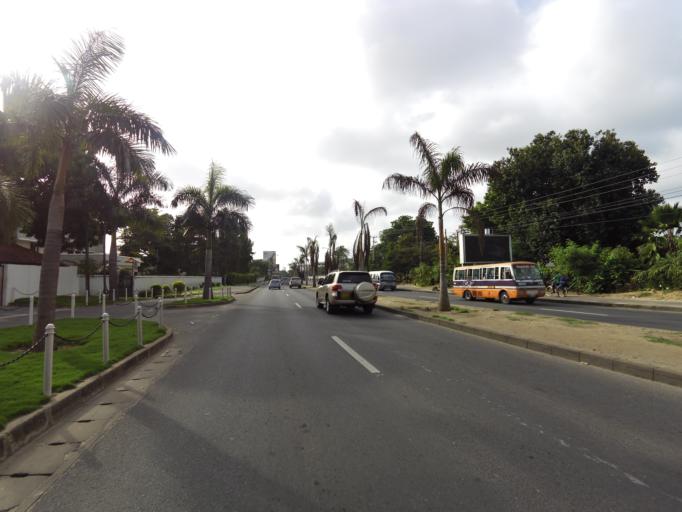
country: TZ
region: Dar es Salaam
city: Magomeni
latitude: -6.7873
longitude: 39.2783
